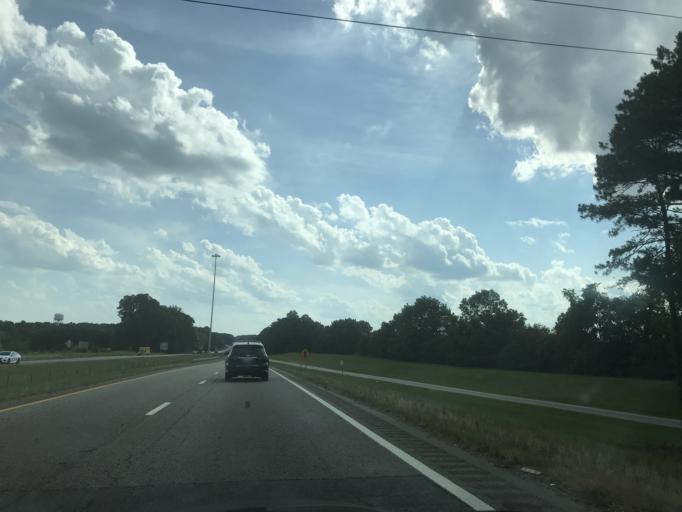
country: US
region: North Carolina
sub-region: Nash County
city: Nashville
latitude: 35.9800
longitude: -77.9756
